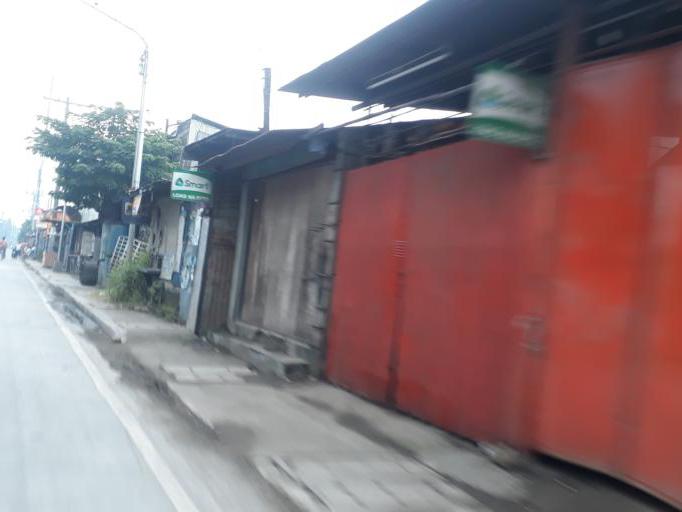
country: PH
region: Metro Manila
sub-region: Caloocan City
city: Niugan
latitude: 14.6793
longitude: 120.9616
